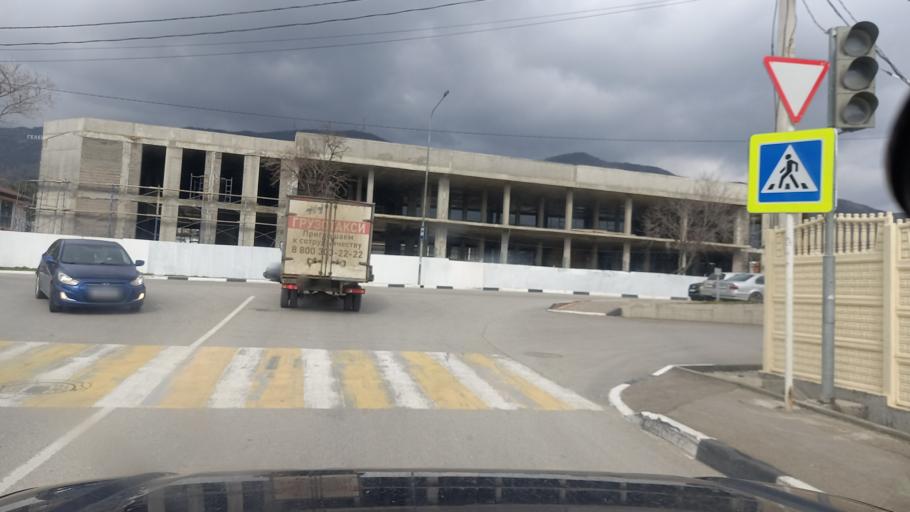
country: RU
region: Krasnodarskiy
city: Gelendzhik
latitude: 44.5608
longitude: 38.0926
